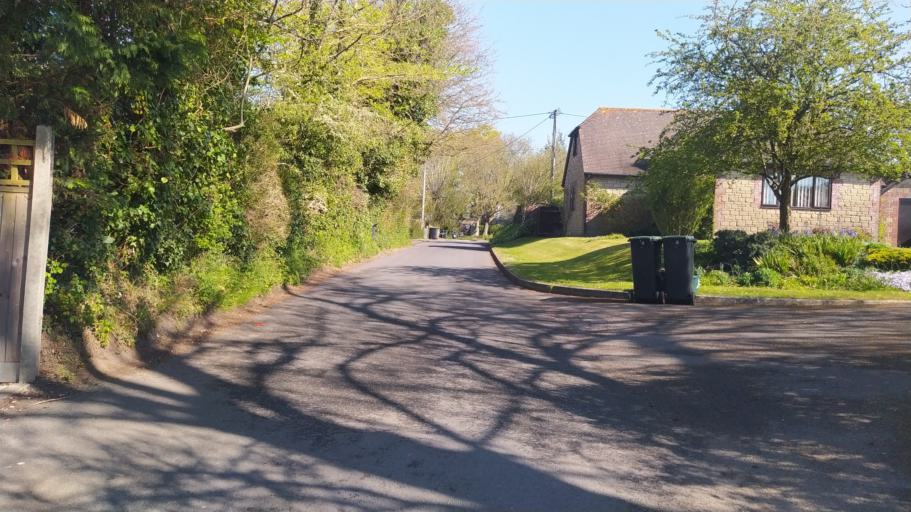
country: GB
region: England
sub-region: Dorset
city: Manston
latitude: 50.9119
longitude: -2.2408
